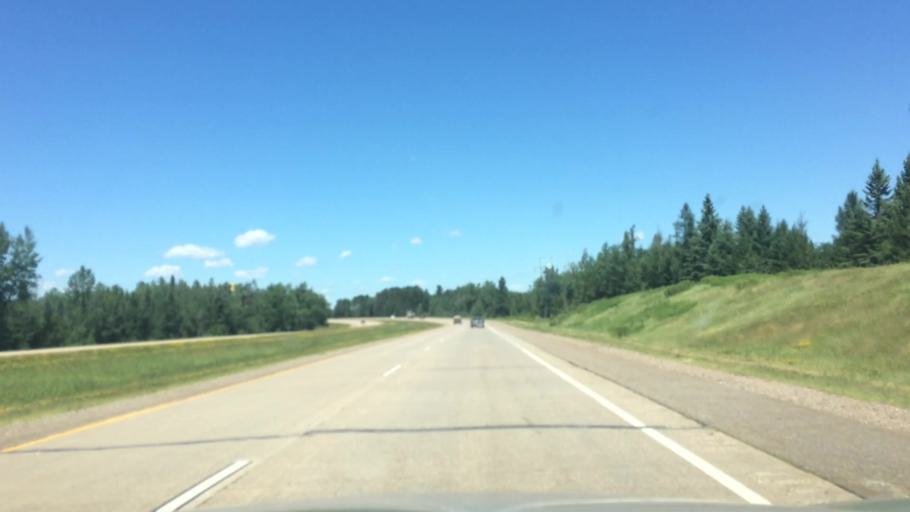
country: US
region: Wisconsin
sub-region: Lincoln County
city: Tomahawk
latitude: 45.3712
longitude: -89.6668
